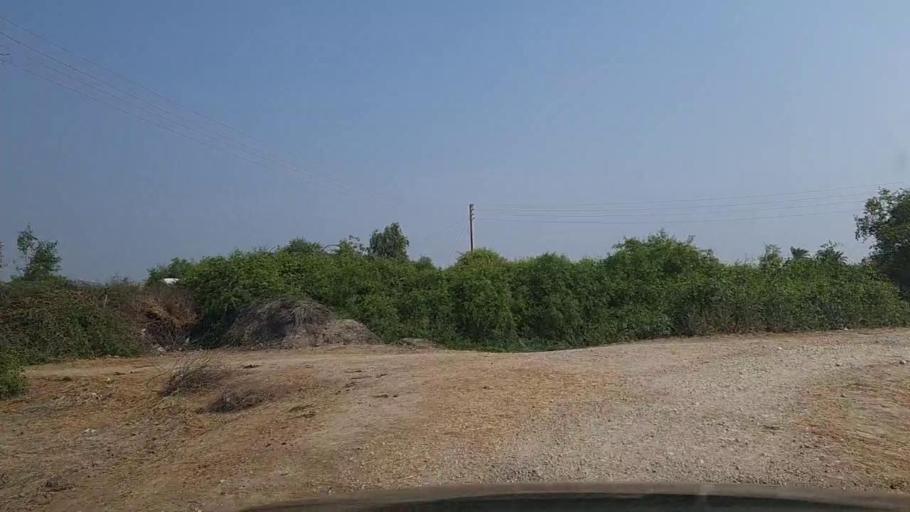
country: PK
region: Sindh
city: Mirpur Batoro
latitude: 24.6857
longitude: 68.2222
